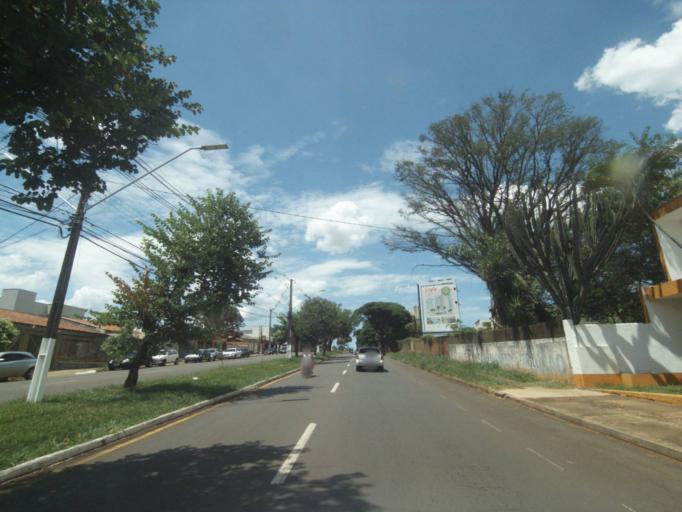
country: BR
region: Parana
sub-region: Londrina
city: Londrina
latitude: -23.3091
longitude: -51.2029
